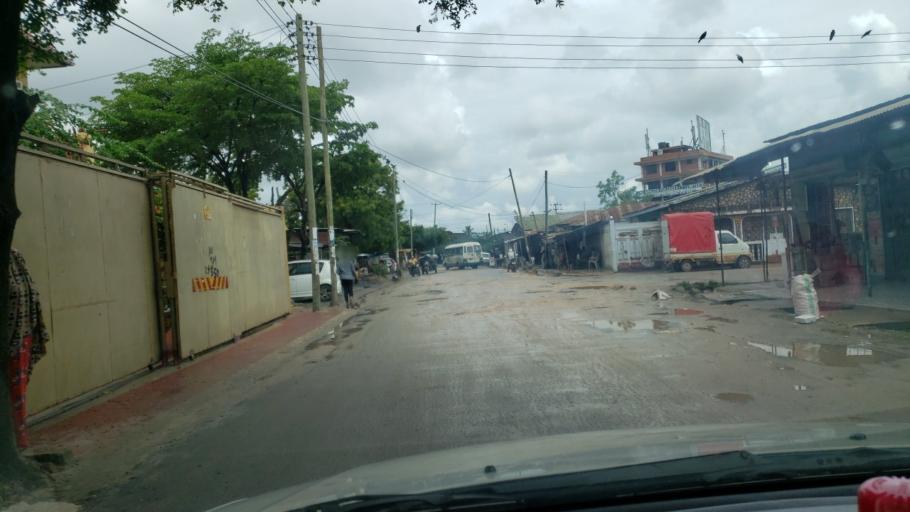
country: TZ
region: Dar es Salaam
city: Magomeni
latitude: -6.8049
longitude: 39.2459
